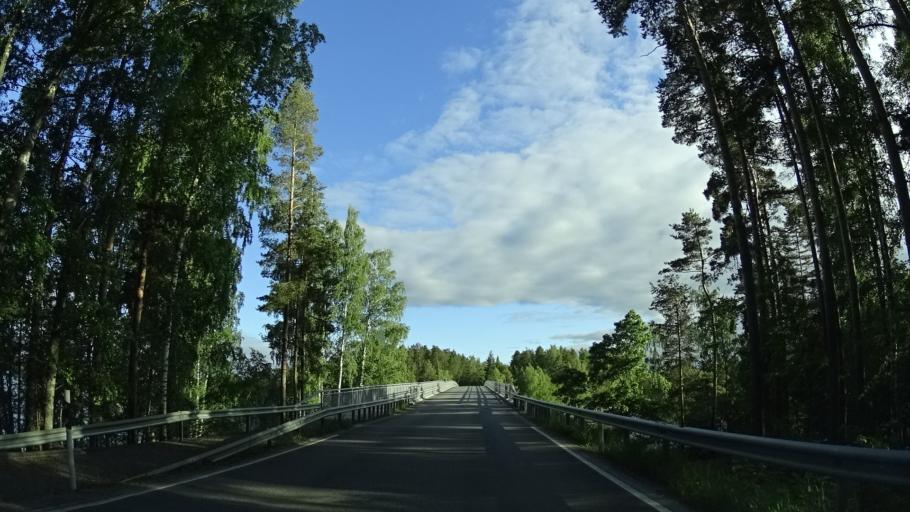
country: FI
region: Paijanne Tavastia
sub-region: Lahti
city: Asikkala
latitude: 61.3199
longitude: 25.5554
